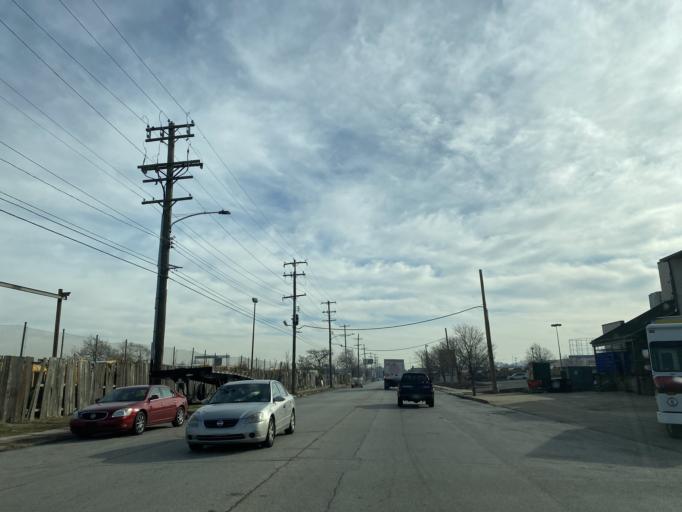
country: US
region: New Jersey
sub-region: Camden County
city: Pennsauken
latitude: 39.9949
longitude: -75.0912
